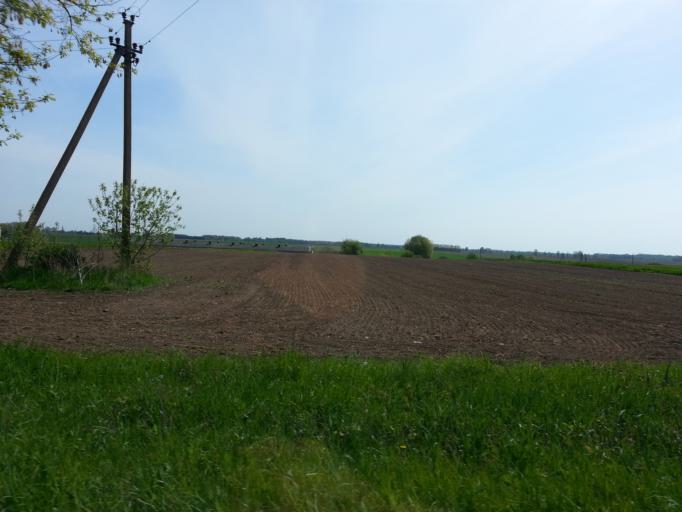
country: LT
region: Panevezys
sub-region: Panevezys City
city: Panevezys
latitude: 55.8943
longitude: 24.2361
